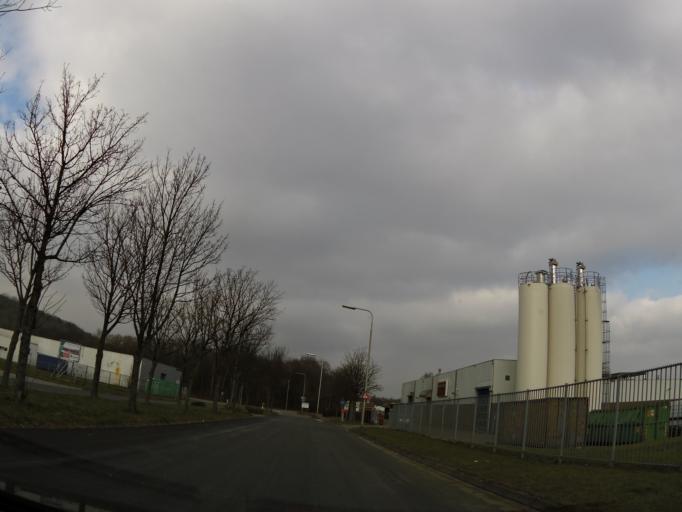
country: NL
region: Limburg
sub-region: Gemeente Kerkrade
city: Kerkrade
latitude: 50.8702
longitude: 6.0322
